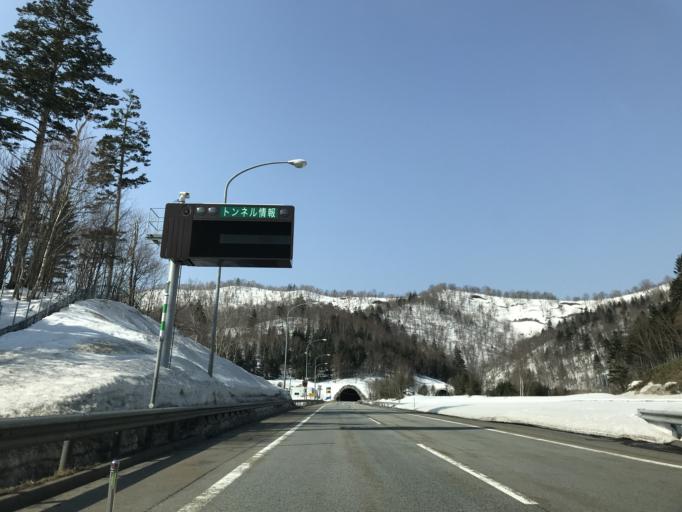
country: JP
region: Hokkaido
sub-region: Asahikawa-shi
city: Asahikawa
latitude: 43.7859
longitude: 142.2385
